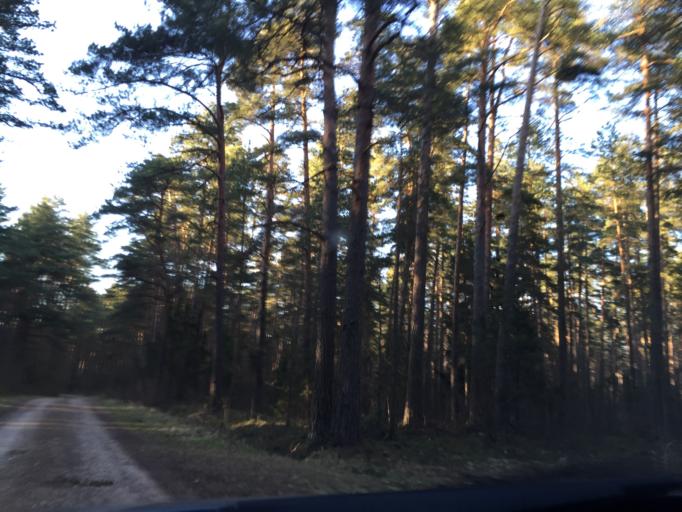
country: LV
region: Kekava
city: Kekava
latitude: 56.8634
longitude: 24.2235
